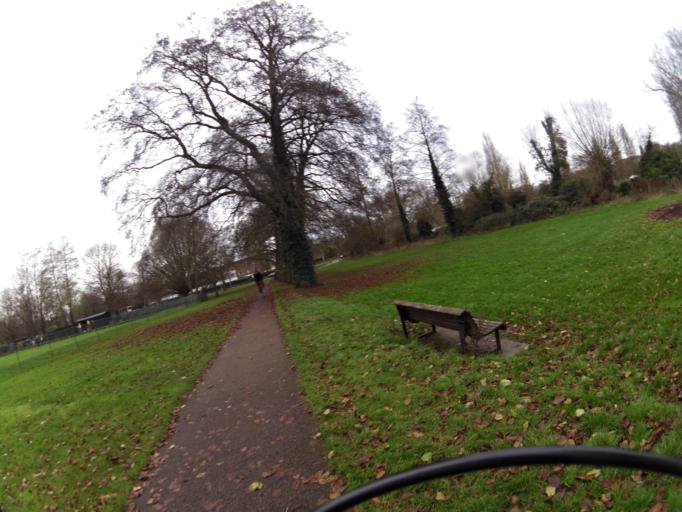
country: GB
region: England
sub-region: Cambridgeshire
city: Cambridge
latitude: 52.1971
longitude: 0.1143
